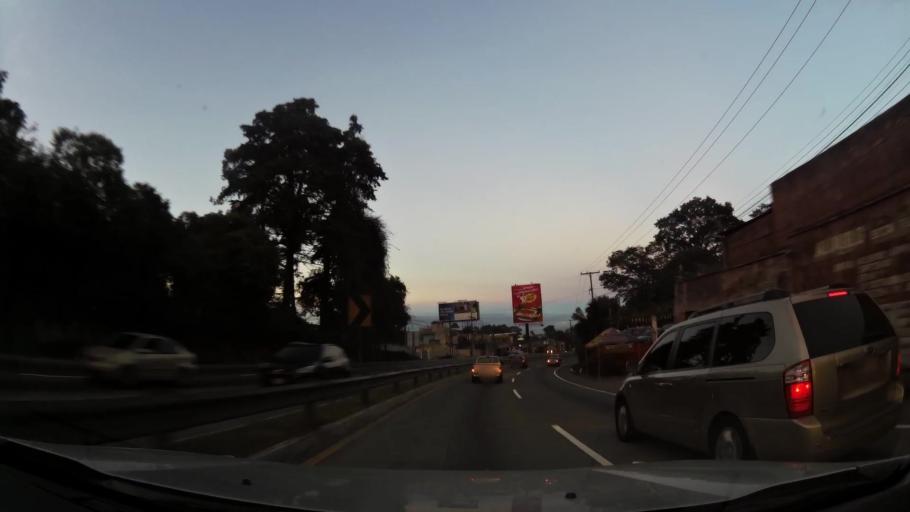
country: GT
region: Guatemala
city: Mixco
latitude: 14.6206
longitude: -90.6157
